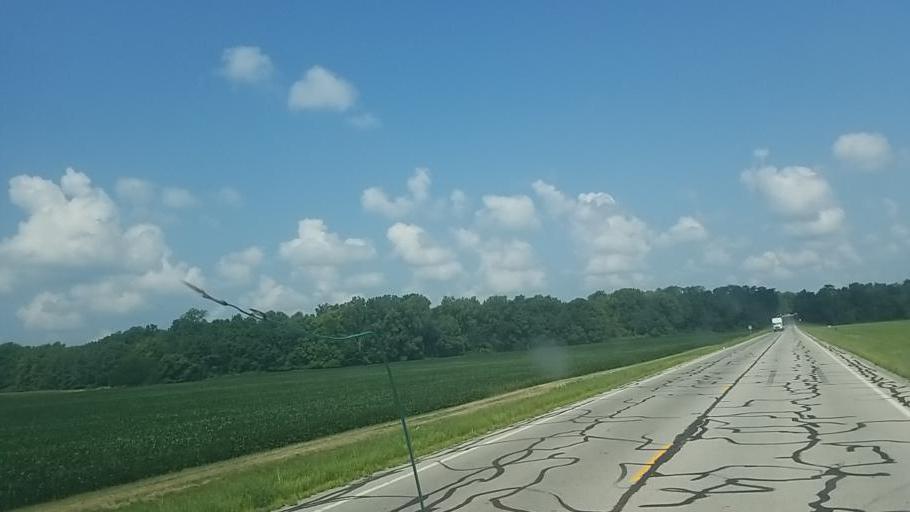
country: US
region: Ohio
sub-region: Wyandot County
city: Upper Sandusky
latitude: 40.8086
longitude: -83.2755
